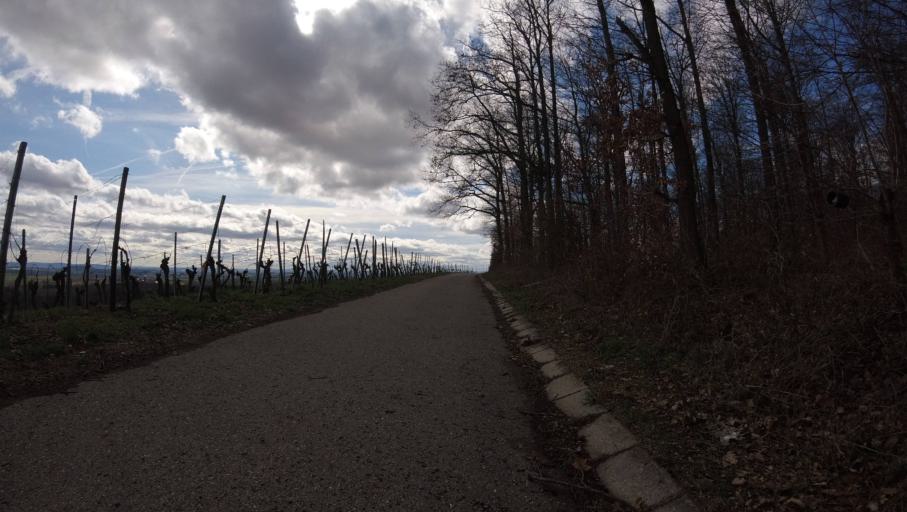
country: DE
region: Baden-Wuerttemberg
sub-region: Regierungsbezirk Stuttgart
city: Grossbottwar
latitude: 48.9933
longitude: 9.3164
